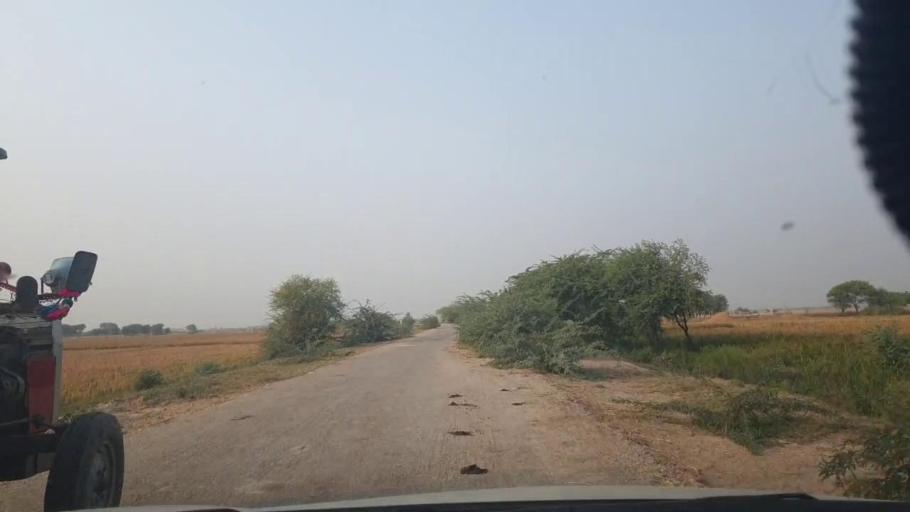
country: PK
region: Sindh
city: Bulri
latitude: 24.8106
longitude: 68.4086
